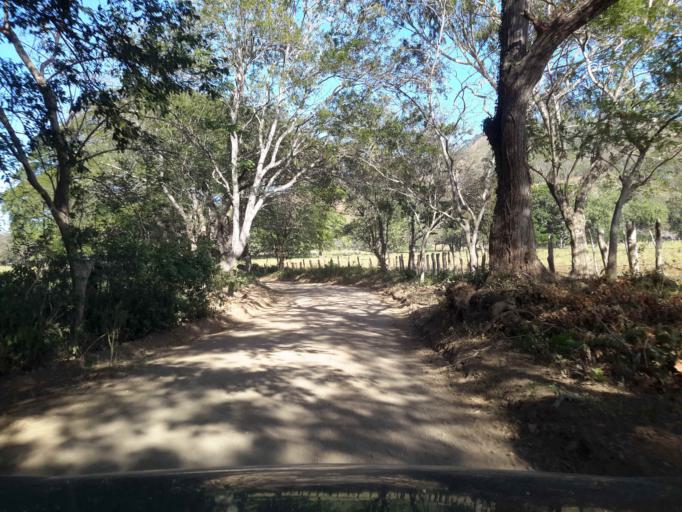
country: NI
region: Rivas
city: San Juan del Sur
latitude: 11.1969
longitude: -85.8068
